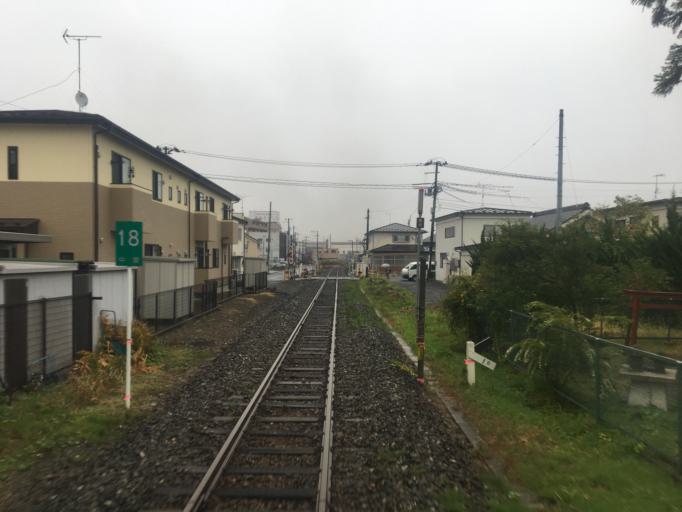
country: JP
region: Miyagi
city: Furukawa
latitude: 38.5711
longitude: 140.9602
